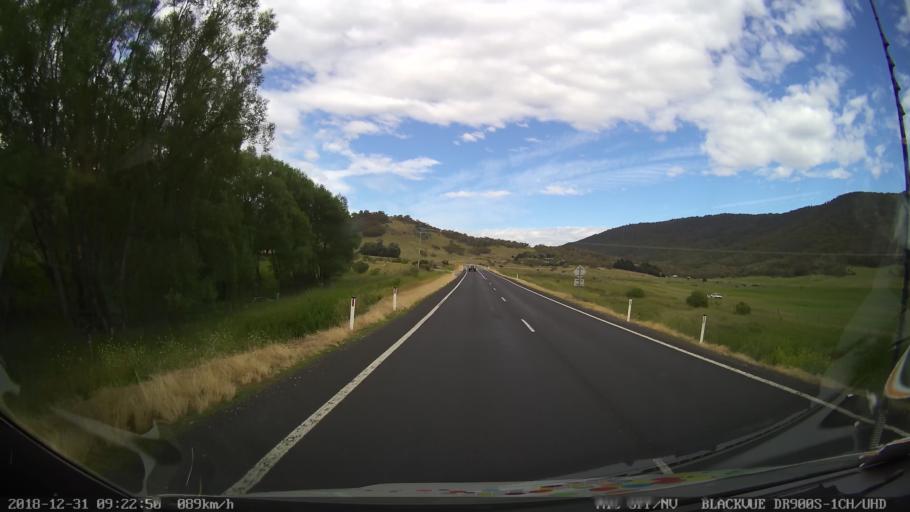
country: AU
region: New South Wales
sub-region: Snowy River
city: Jindabyne
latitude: -36.4369
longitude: 148.5421
